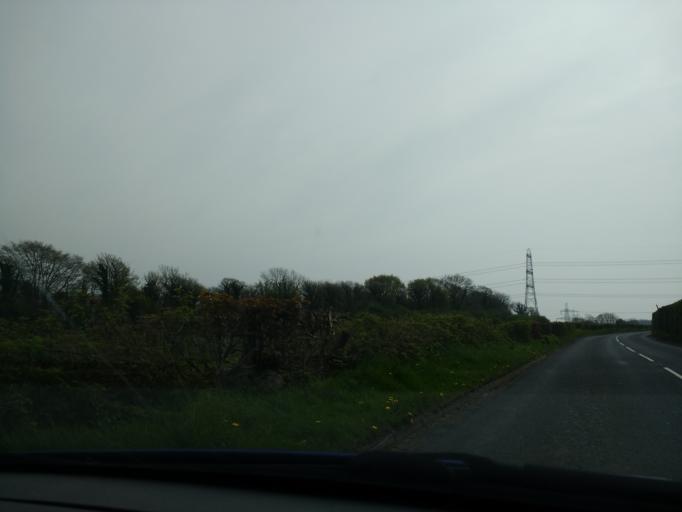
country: GB
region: England
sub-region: Lancashire
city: Lancaster
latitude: 54.0226
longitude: -2.8096
